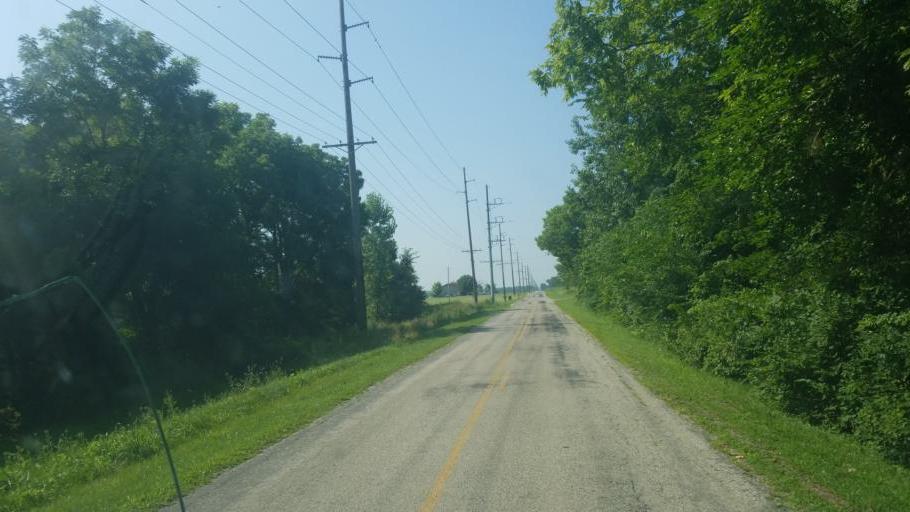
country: US
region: Ohio
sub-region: Wyandot County
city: Upper Sandusky
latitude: 40.6633
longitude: -83.3241
